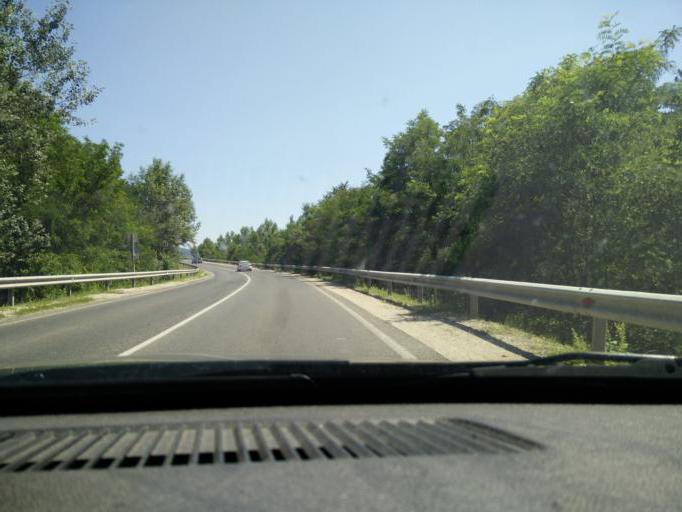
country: HU
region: Komarom-Esztergom
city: Baj
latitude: 47.6321
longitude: 18.3560
